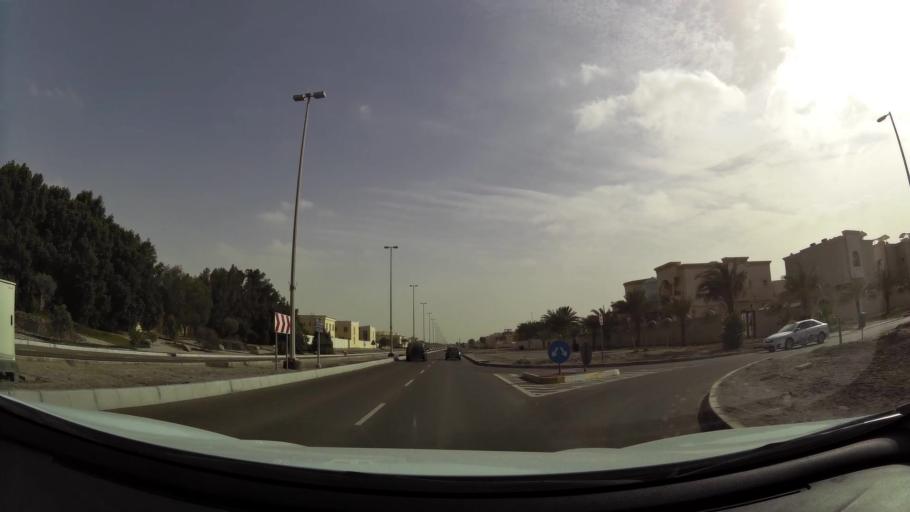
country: AE
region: Abu Dhabi
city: Abu Dhabi
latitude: 24.4139
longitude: 54.6028
